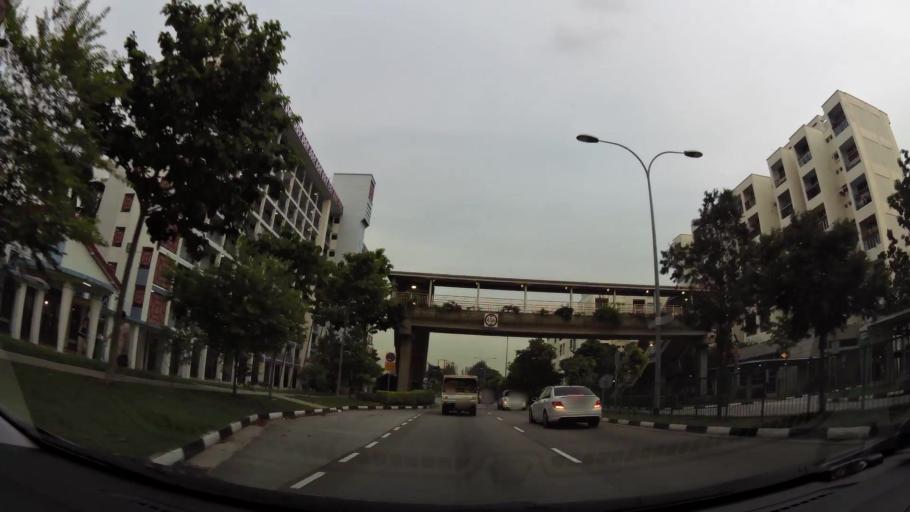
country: SG
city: Singapore
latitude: 1.3082
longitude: 103.8878
